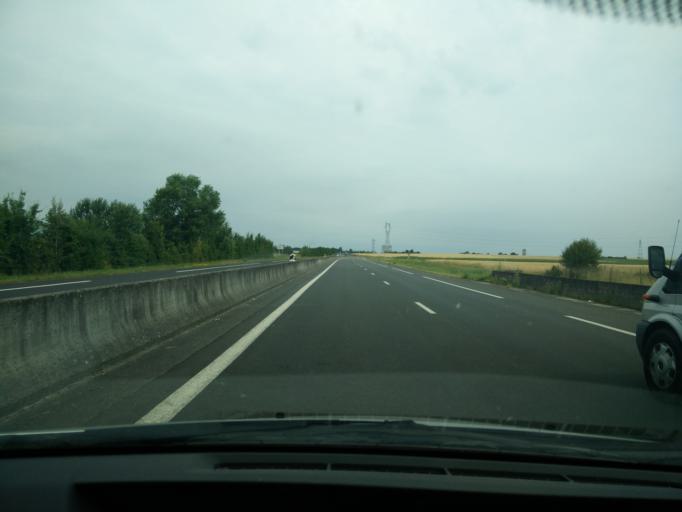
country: FR
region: Pays de la Loire
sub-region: Departement de Maine-et-Loire
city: Doue-la-Fontaine
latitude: 47.2217
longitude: -0.3069
